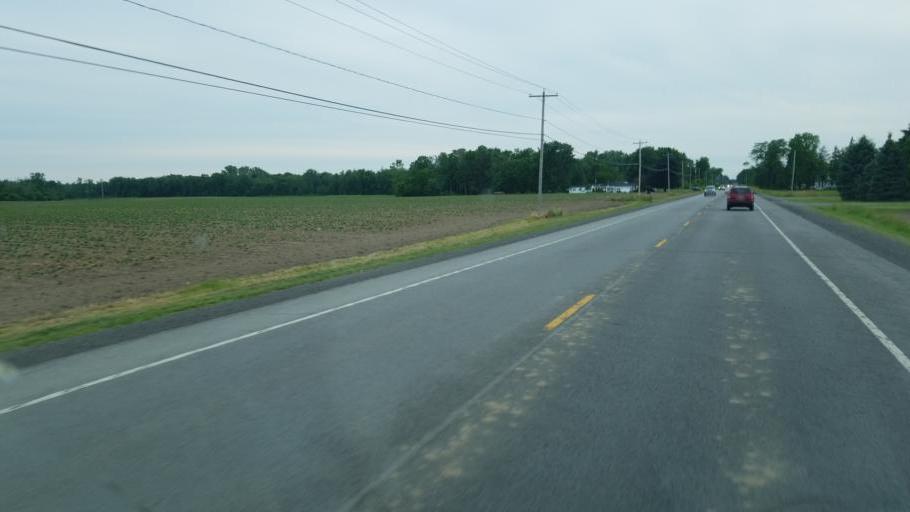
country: US
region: New York
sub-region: Genesee County
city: Oakfield
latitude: 43.0004
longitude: -78.2659
